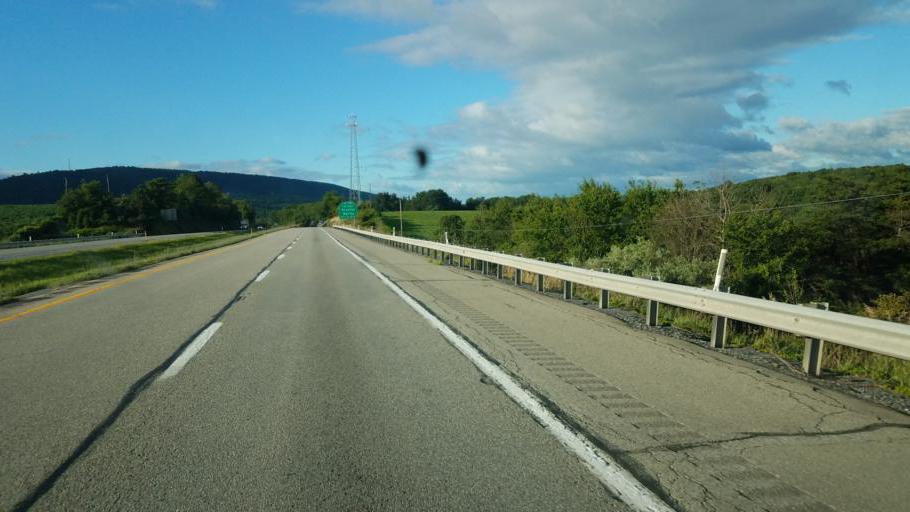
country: US
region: Pennsylvania
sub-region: Bedford County
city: Earlston
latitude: 39.9690
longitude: -78.2467
